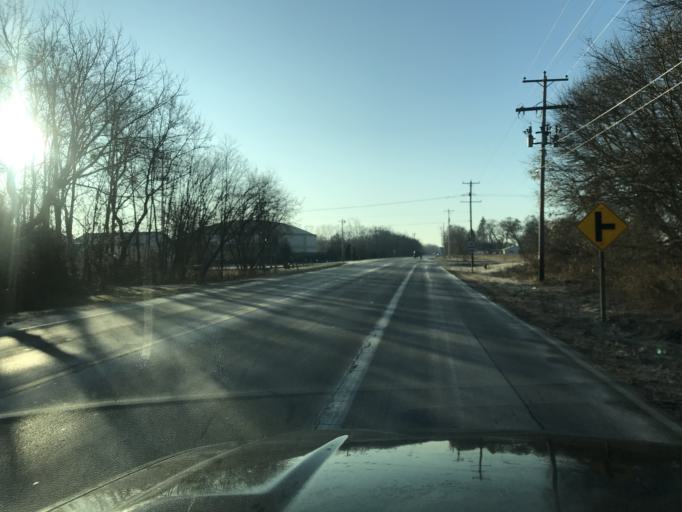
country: US
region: Illinois
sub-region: Lake County
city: Winthrop Harbor
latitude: 42.5231
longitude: -87.8242
